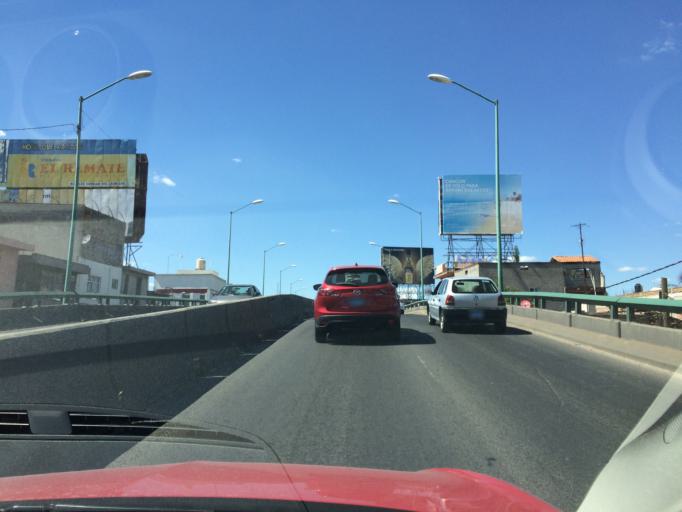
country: MX
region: Guanajuato
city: Leon
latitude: 21.1158
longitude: -101.6864
